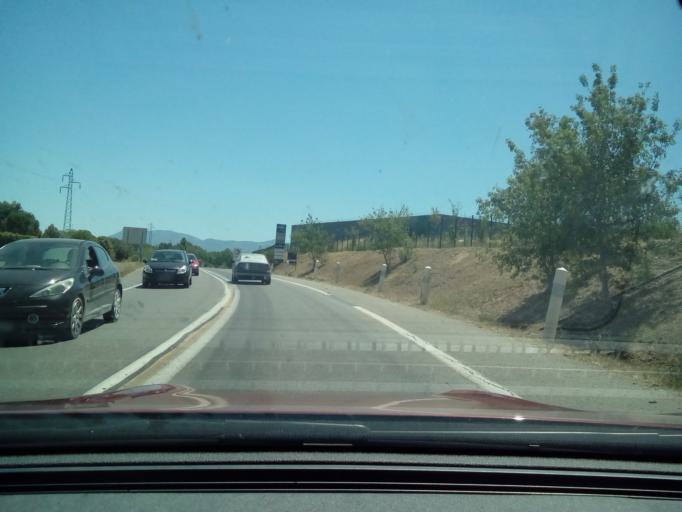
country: FR
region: Provence-Alpes-Cote d'Azur
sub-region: Departement des Bouches-du-Rhone
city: Rousset
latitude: 43.4686
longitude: 5.5984
